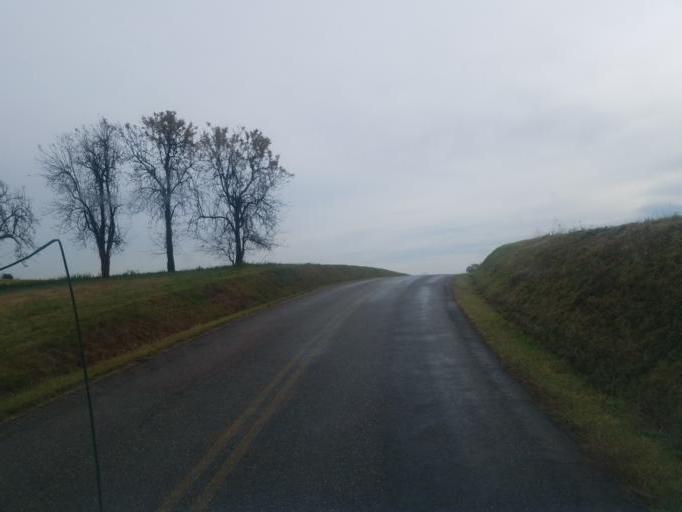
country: US
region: Ohio
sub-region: Washington County
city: Beverly
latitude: 39.5532
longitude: -81.6783
